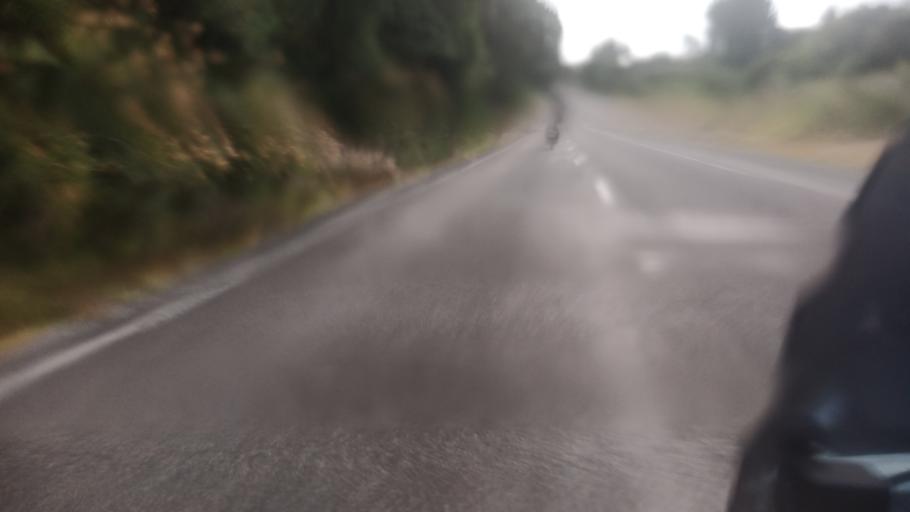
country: NZ
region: Bay of Plenty
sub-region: Opotiki District
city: Opotiki
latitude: -37.9791
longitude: 177.4333
